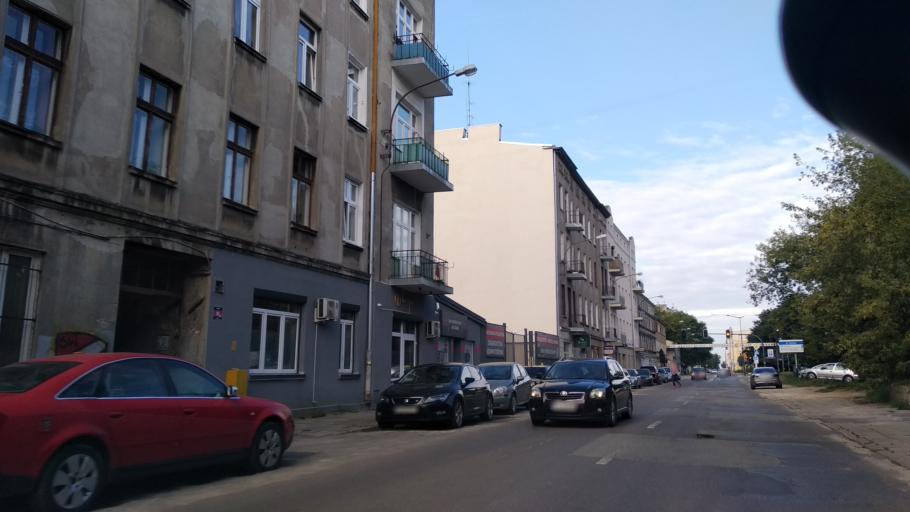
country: PL
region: Lodz Voivodeship
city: Lodz
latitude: 51.7671
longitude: 19.4751
